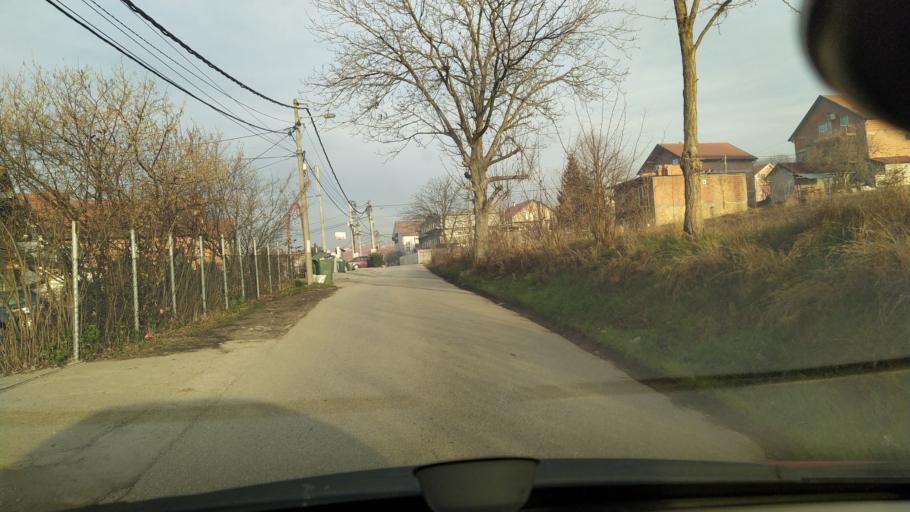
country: RS
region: Central Serbia
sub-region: Belgrade
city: Zvezdara
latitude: 44.7487
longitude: 20.5746
